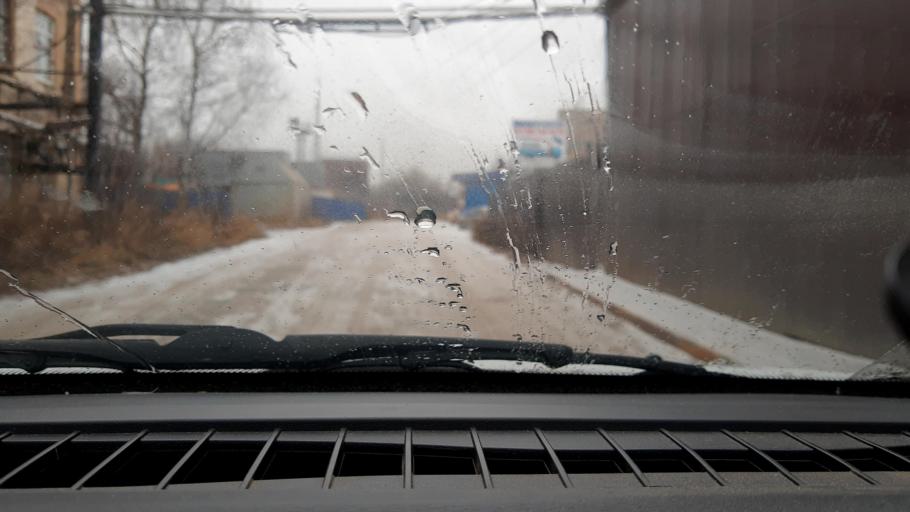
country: RU
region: Nizjnij Novgorod
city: Nizhniy Novgorod
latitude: 56.3364
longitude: 43.8897
